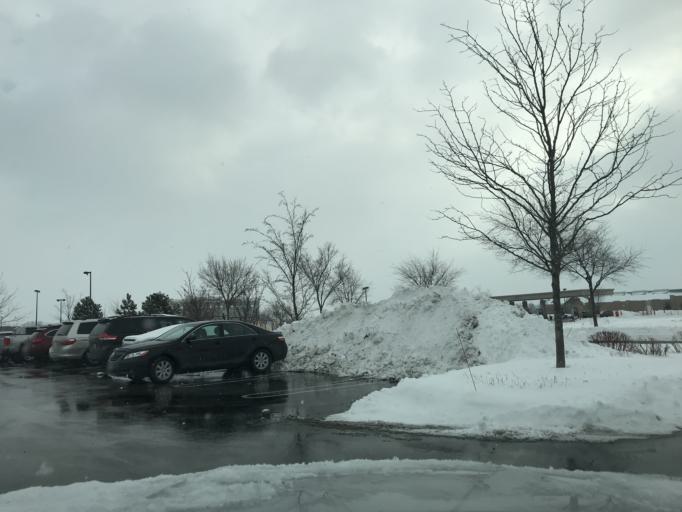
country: US
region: Wisconsin
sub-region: Dane County
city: Sun Prairie
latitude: 43.1672
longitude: -89.2747
